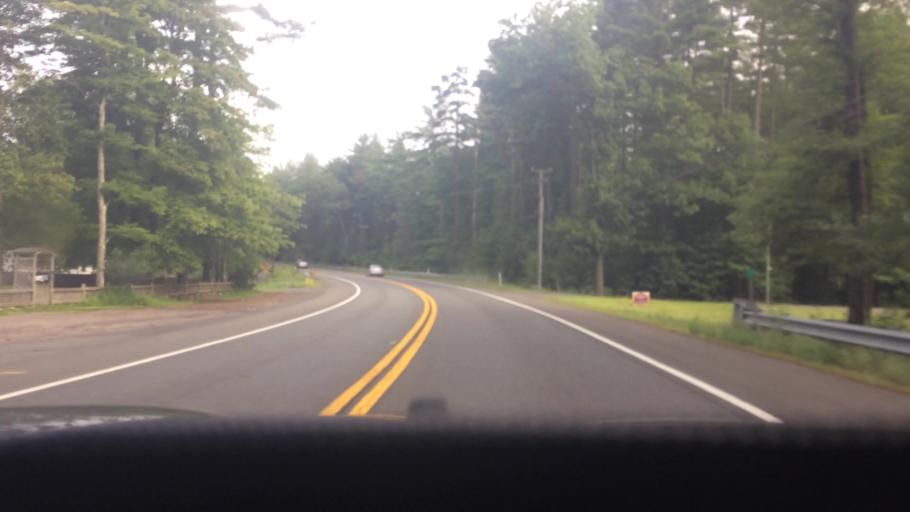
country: US
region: Massachusetts
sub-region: Franklin County
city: Millers Falls
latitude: 42.6065
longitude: -72.5036
